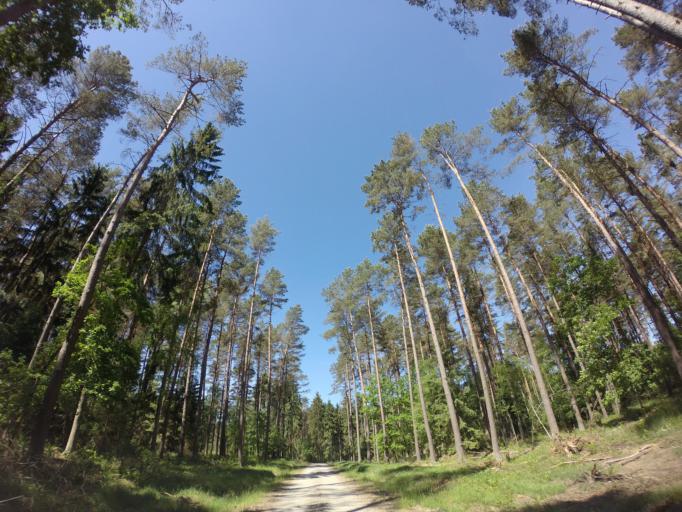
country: PL
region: West Pomeranian Voivodeship
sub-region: Powiat choszczenski
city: Recz
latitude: 53.2940
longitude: 15.6303
